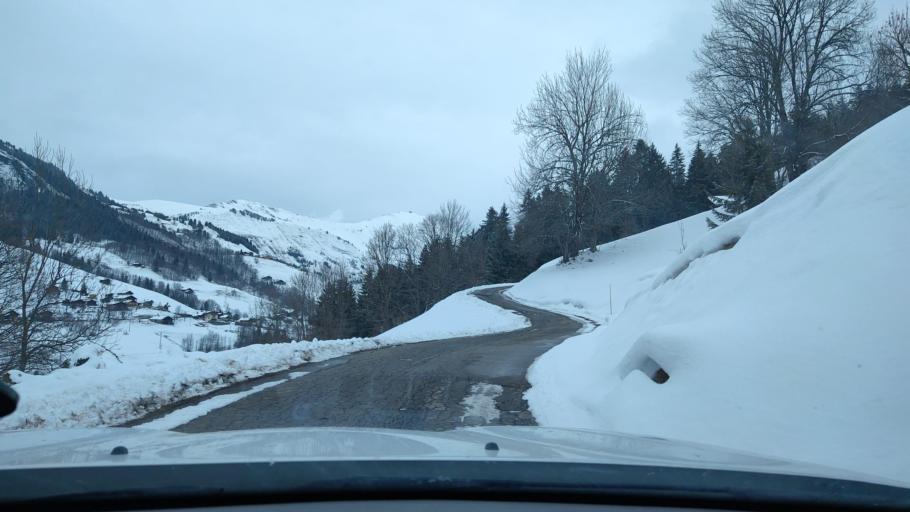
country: FR
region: Rhone-Alpes
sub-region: Departement de la Savoie
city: Beaufort
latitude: 45.7514
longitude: 6.5996
